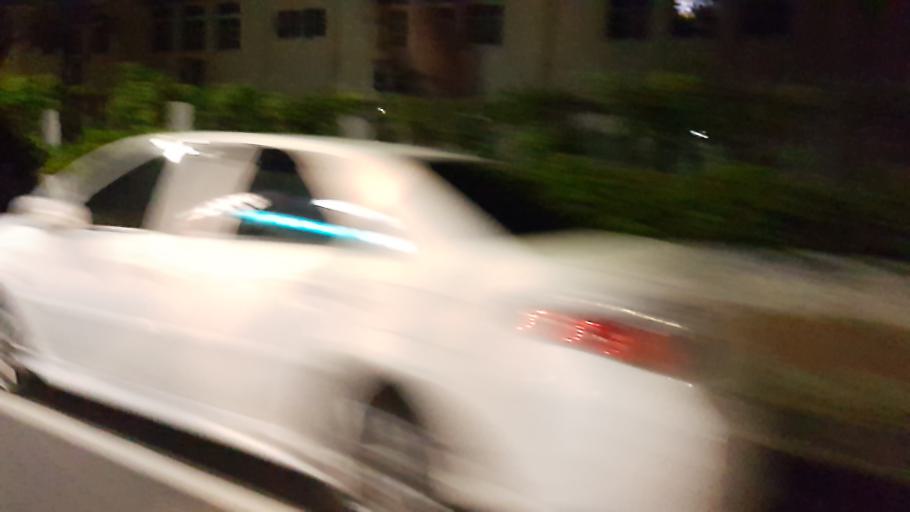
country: TW
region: Taiwan
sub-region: Hsinchu
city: Hsinchu
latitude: 24.8021
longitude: 120.9593
